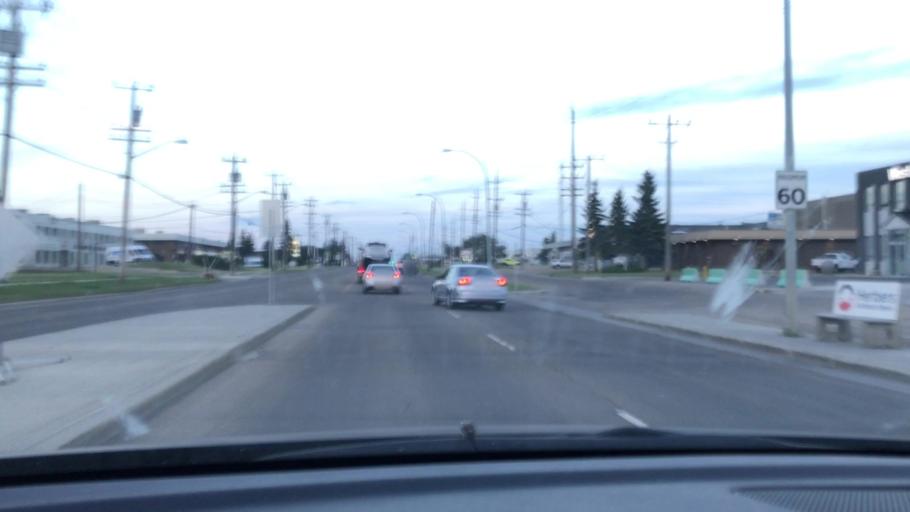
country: CA
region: Alberta
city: Edmonton
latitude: 53.4882
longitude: -113.4846
